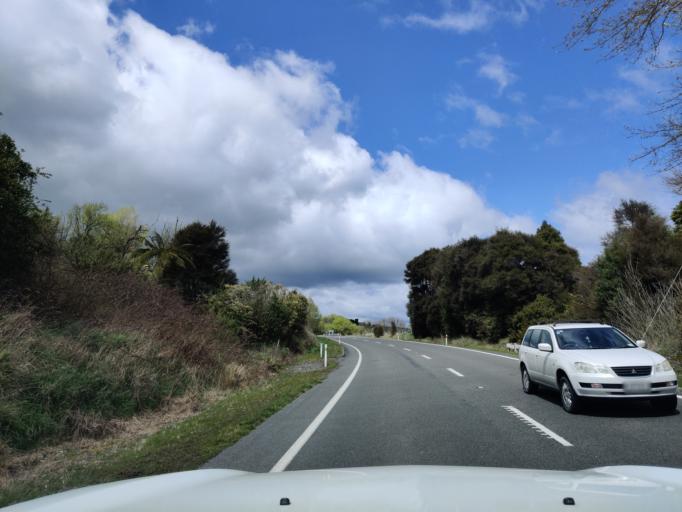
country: NZ
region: Manawatu-Wanganui
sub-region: Ruapehu District
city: Waiouru
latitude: -39.6490
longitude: 175.3246
